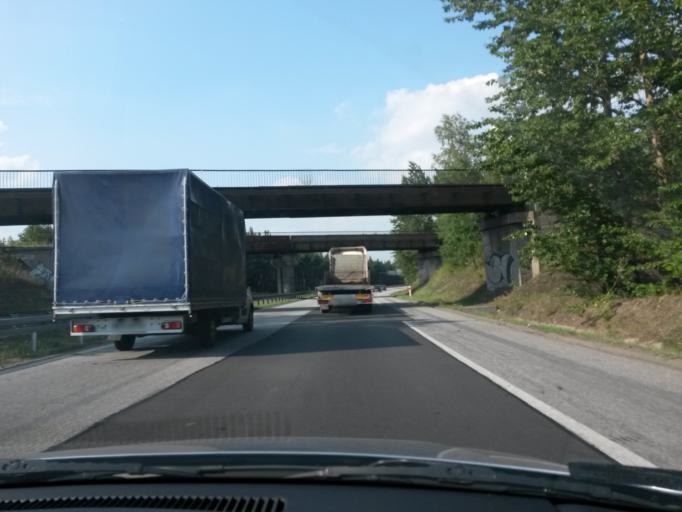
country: PL
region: Silesian Voivodeship
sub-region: Myslowice
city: Myslowice
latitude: 50.2299
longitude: 19.1676
